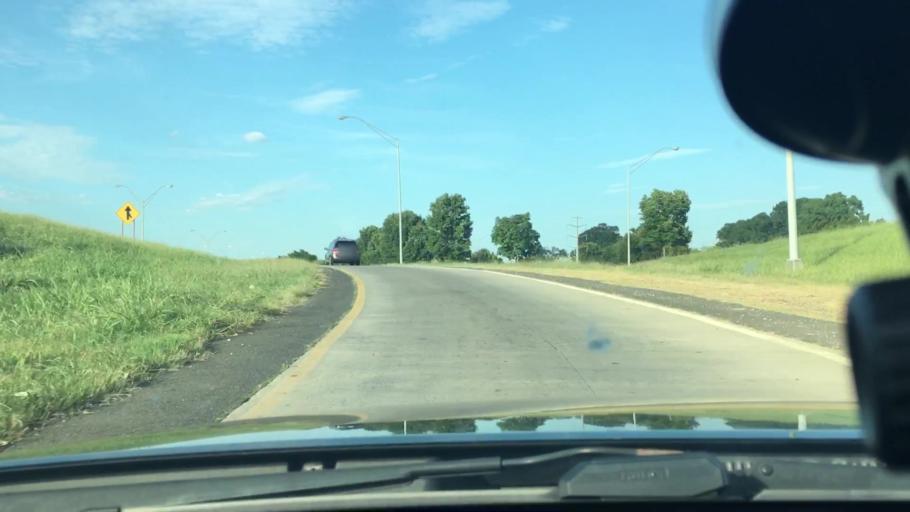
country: US
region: North Carolina
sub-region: Mecklenburg County
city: Charlotte
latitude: 35.2148
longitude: -80.8375
